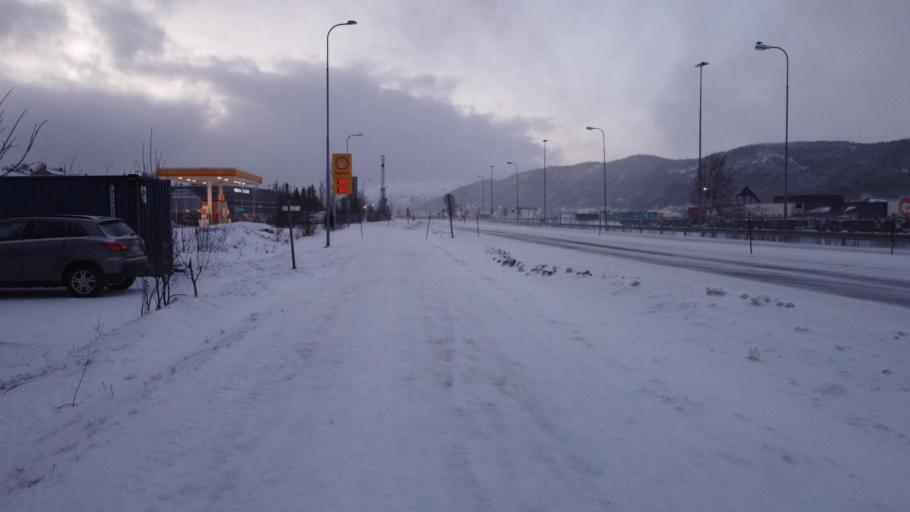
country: NO
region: Nordland
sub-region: Rana
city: Mo i Rana
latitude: 66.3183
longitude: 14.1415
